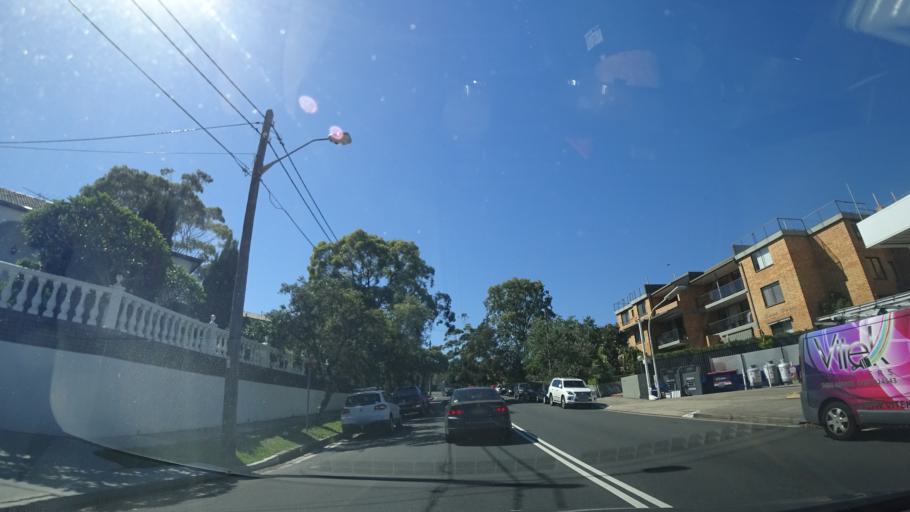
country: AU
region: New South Wales
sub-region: Randwick
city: Randwick
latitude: -33.9090
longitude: 151.2487
